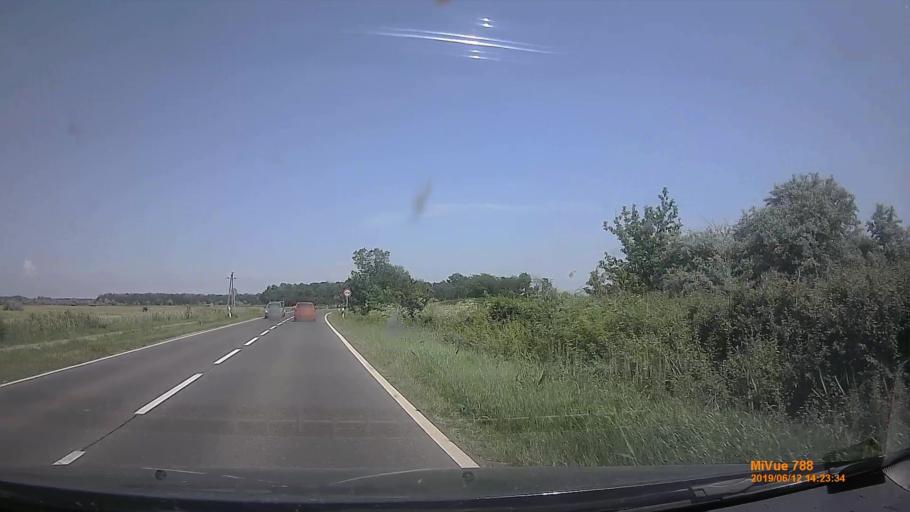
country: HU
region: Csongrad
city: Deszk
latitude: 46.2194
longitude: 20.2950
